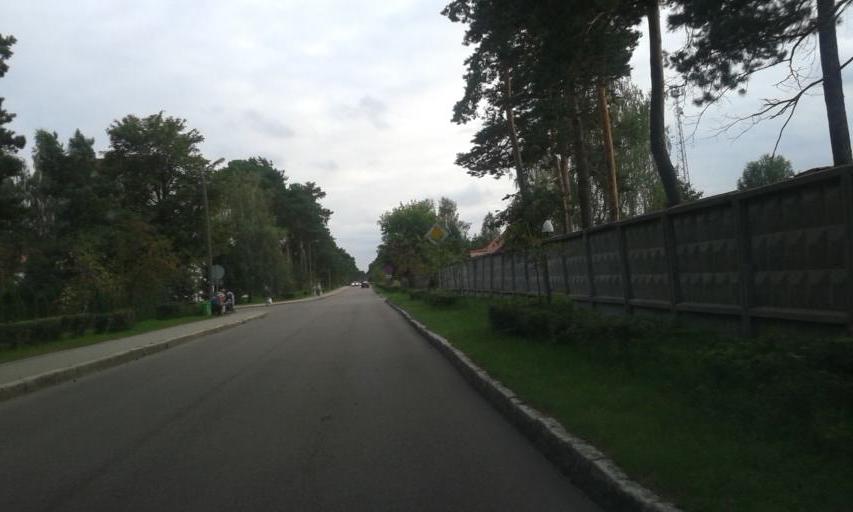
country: PL
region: West Pomeranian Voivodeship
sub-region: Powiat szczecinecki
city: Borne Sulinowo
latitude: 53.5819
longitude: 16.5337
